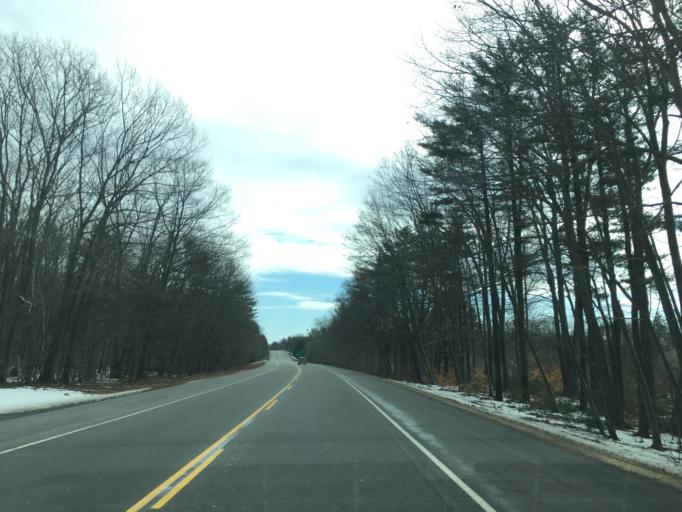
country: US
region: New Hampshire
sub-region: Rockingham County
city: Hampton
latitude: 42.9376
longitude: -70.8471
